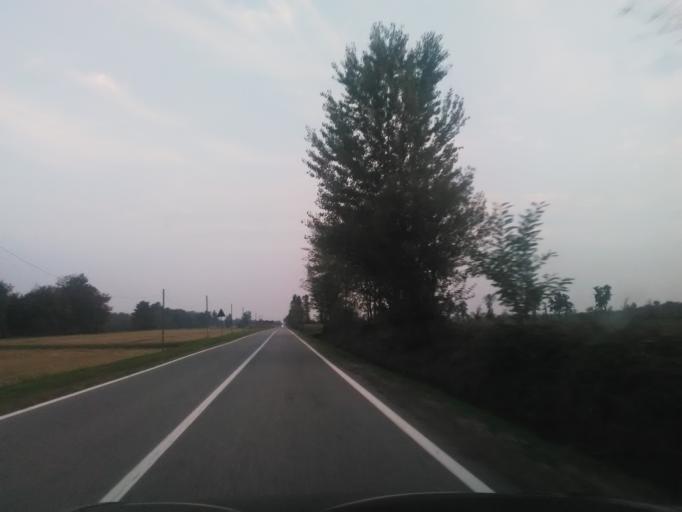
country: IT
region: Piedmont
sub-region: Provincia di Vercelli
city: Rovasenda
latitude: 45.5507
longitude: 8.3016
